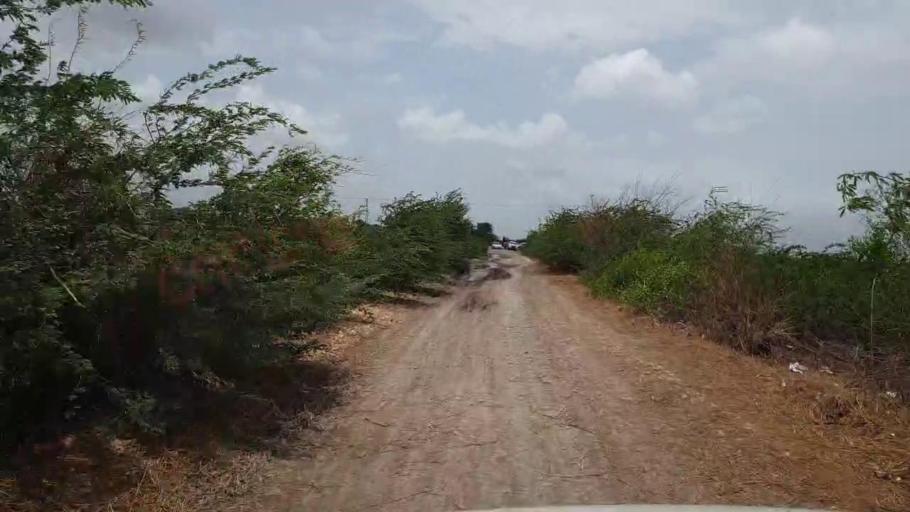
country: PK
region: Sindh
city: Kario
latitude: 24.7239
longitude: 68.5630
